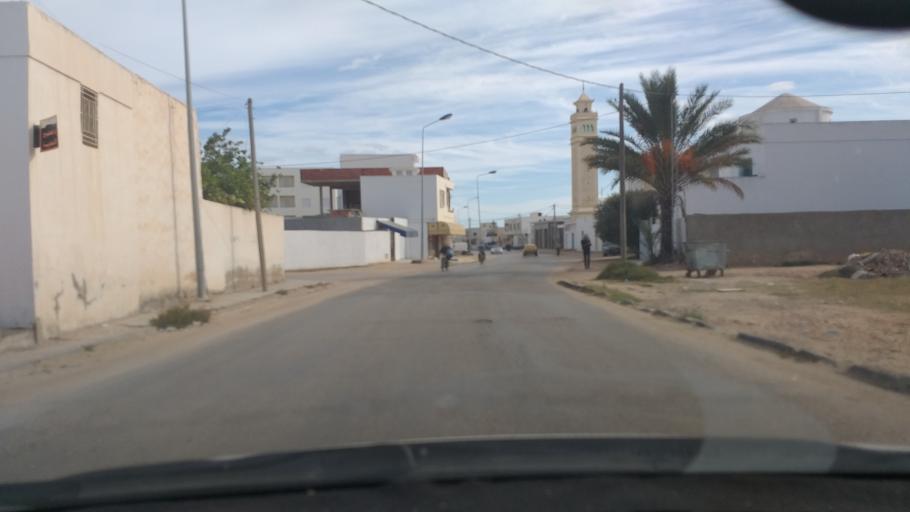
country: TN
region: Safaqis
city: Al Qarmadah
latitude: 34.7966
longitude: 10.7999
